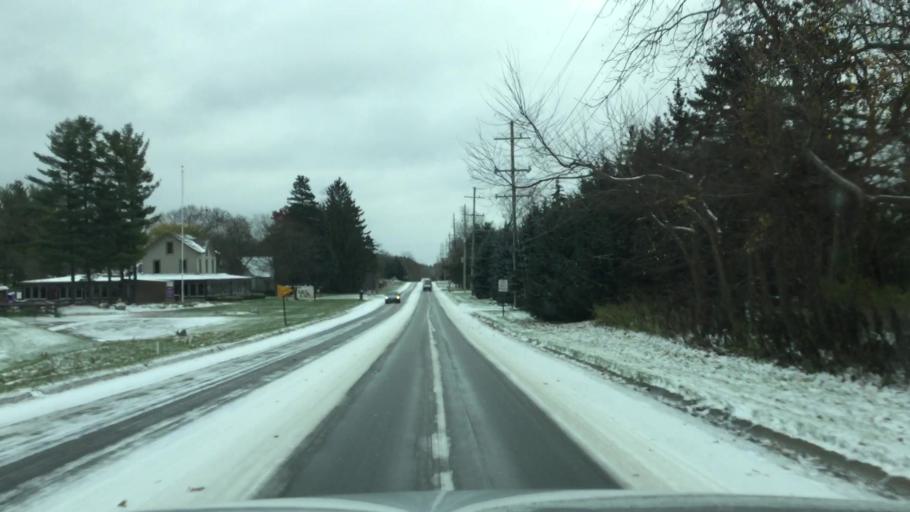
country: US
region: Michigan
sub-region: Livingston County
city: Brighton
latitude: 42.5277
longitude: -83.8473
